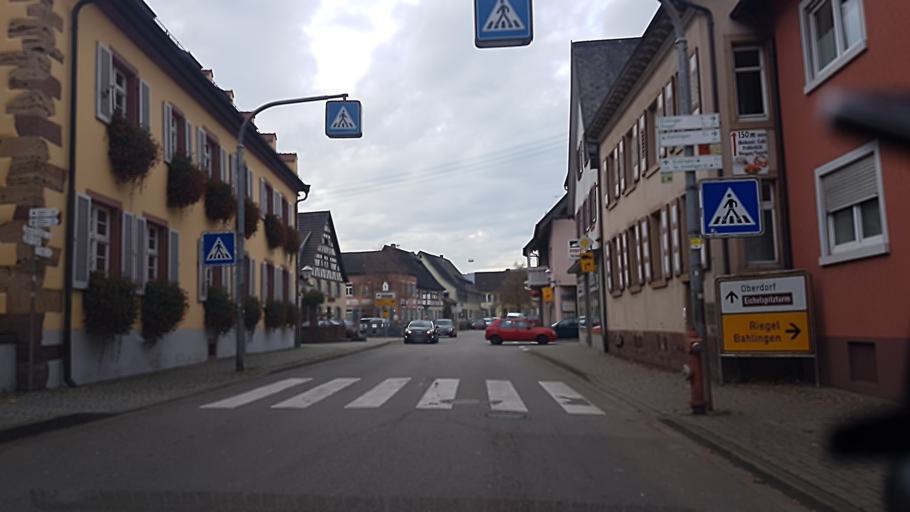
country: DE
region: Baden-Wuerttemberg
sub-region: Freiburg Region
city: Eichstetten
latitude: 48.0942
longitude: 7.7458
